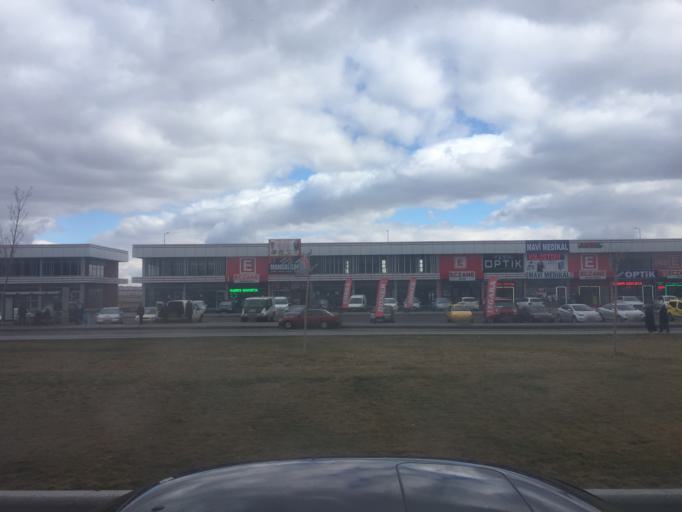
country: TR
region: Kayseri
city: Melikgazi
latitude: 38.7707
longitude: 35.4126
